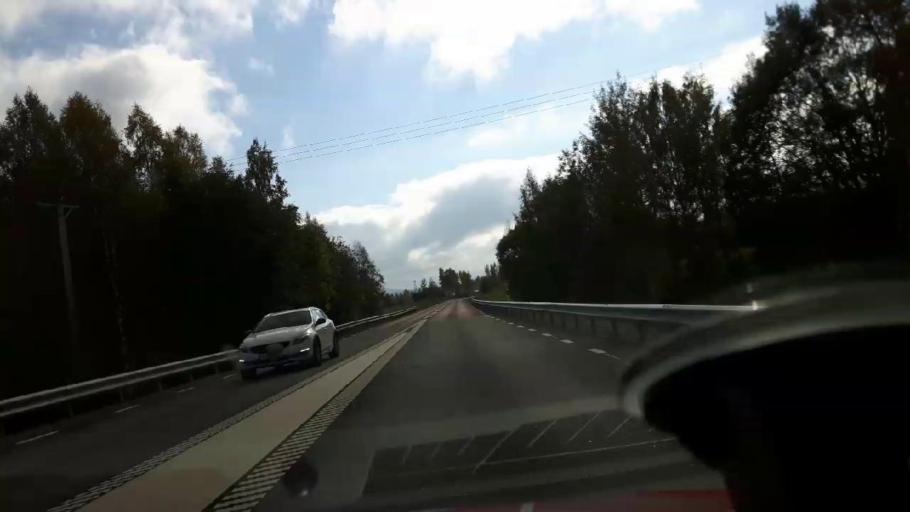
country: SE
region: Gaevleborg
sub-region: Bollnas Kommun
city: Arbra
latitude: 61.5394
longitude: 16.3592
